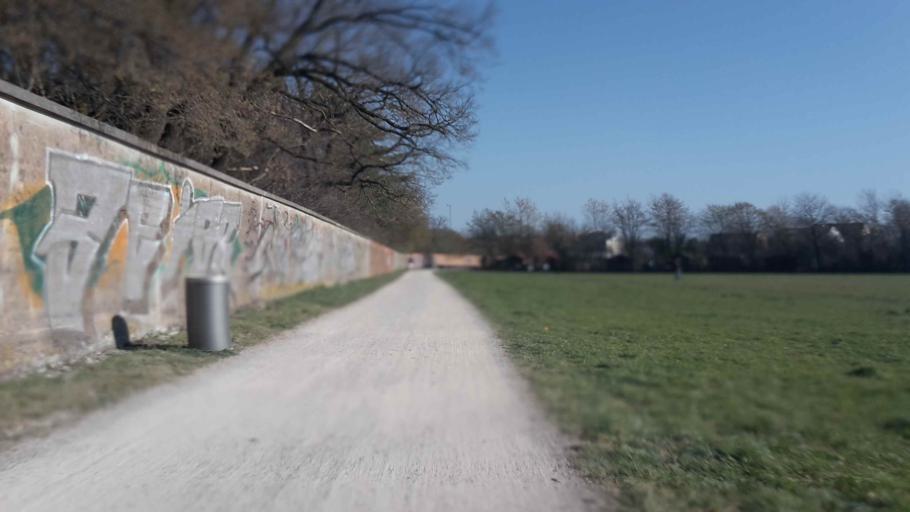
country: DE
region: Bavaria
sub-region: Upper Bavaria
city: Pasing
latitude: 48.1495
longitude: 11.4933
